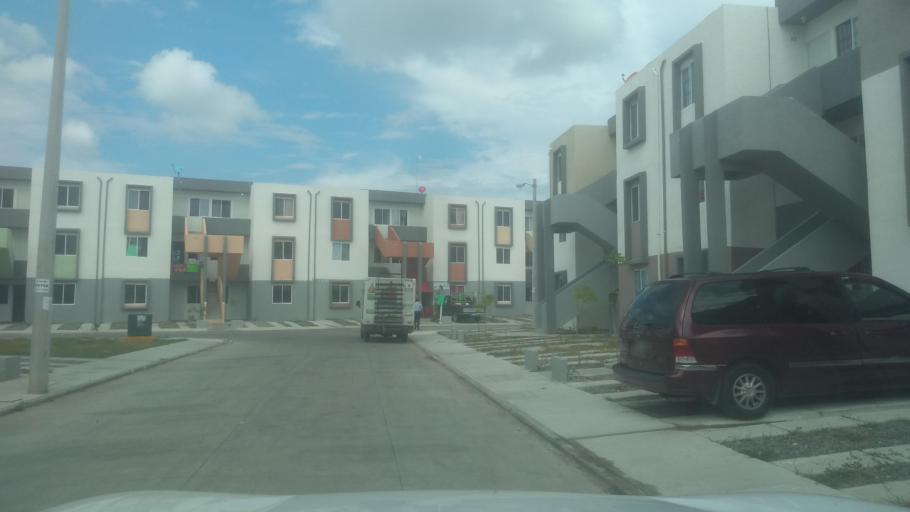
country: MX
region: Veracruz
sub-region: Medellin
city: Fraccionamiento Arboledas San Ramon
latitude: 19.0946
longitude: -96.1704
